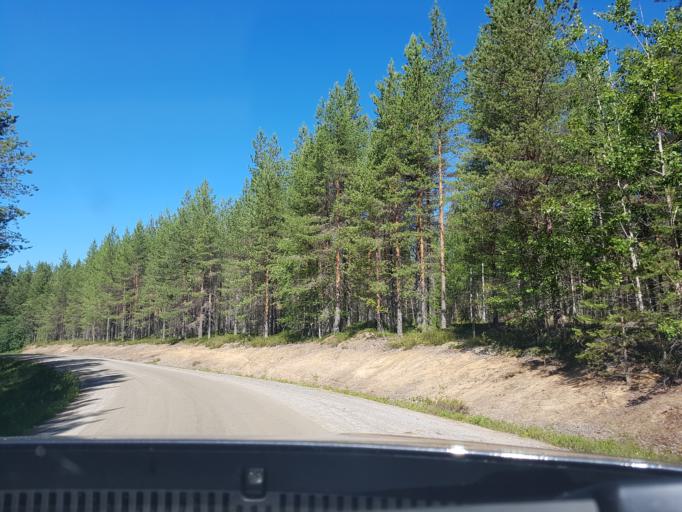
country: FI
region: Kainuu
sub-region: Kehys-Kainuu
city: Kuhmo
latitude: 64.1944
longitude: 29.6045
